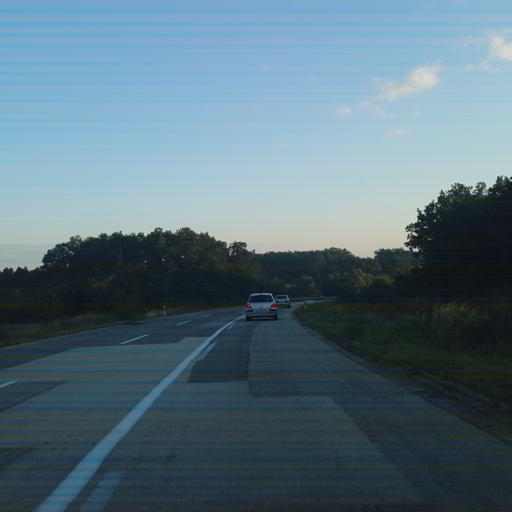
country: RS
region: Central Serbia
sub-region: Zajecarski Okrug
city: Zajecar
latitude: 44.0732
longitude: 22.3334
